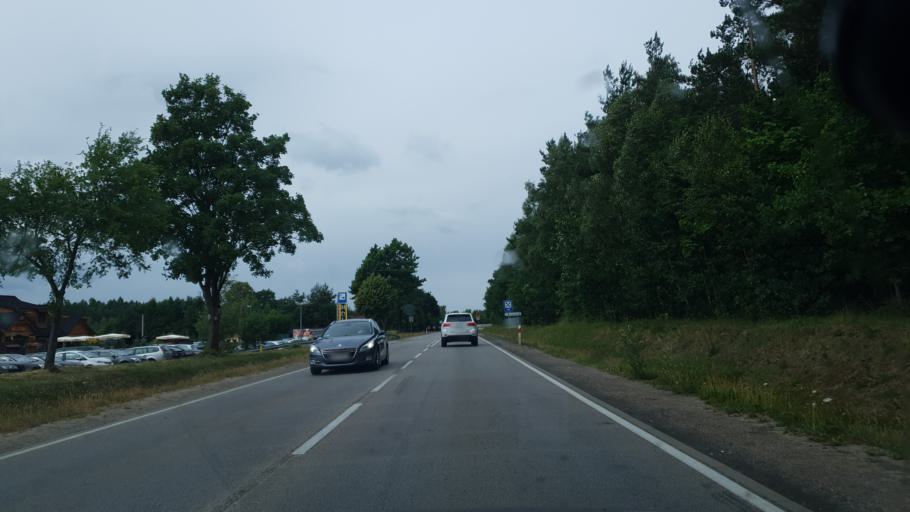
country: PL
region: Pomeranian Voivodeship
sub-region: Powiat kartuski
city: Banino
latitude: 54.3989
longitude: 18.3586
